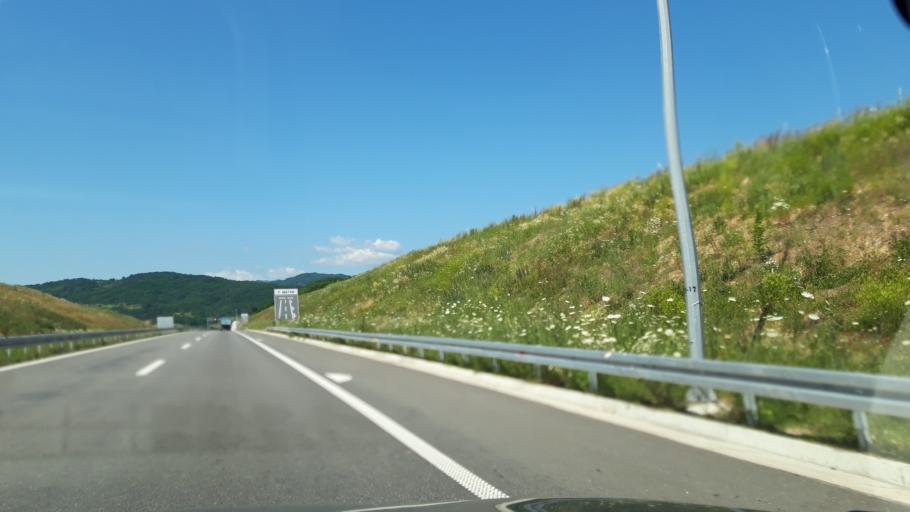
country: RS
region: Central Serbia
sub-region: Pcinjski Okrug
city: Vladicin Han
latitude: 42.7135
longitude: 22.0732
